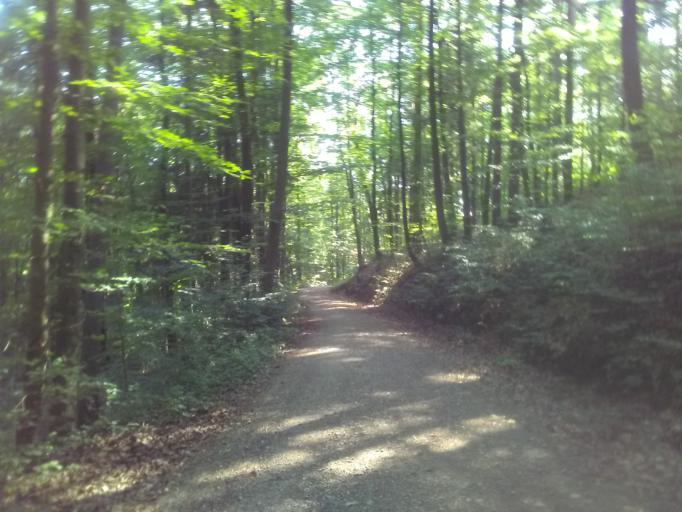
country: DE
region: Bavaria
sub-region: Upper Franconia
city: Bamberg
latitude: 49.8658
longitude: 10.9025
